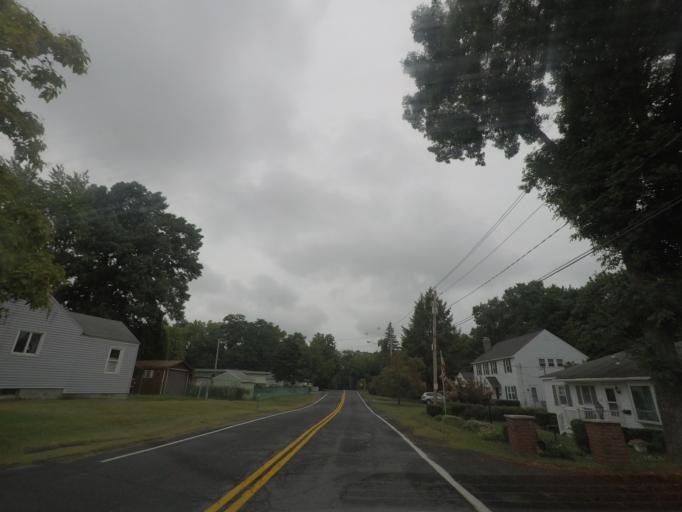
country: US
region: New York
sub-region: Rensselaer County
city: Hampton Manor
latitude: 42.6192
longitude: -73.7181
